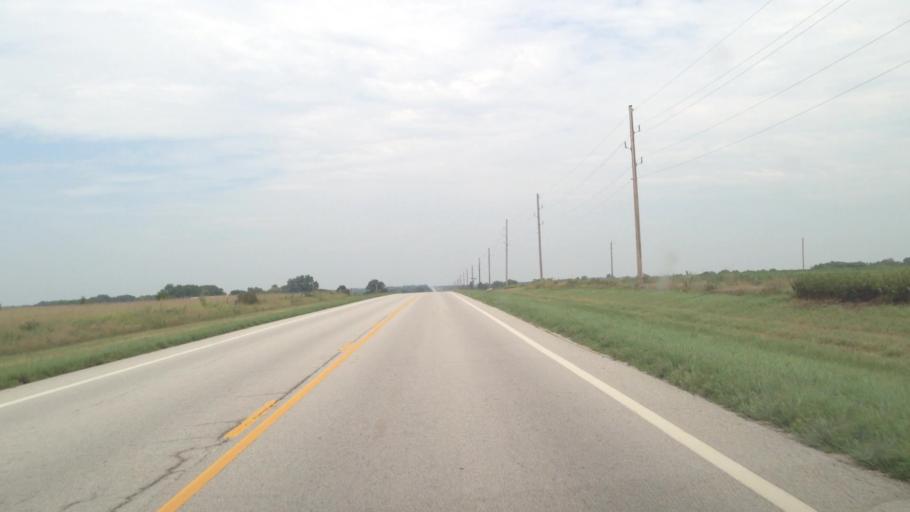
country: US
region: Kansas
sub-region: Allen County
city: Iola
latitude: 37.9342
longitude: -95.1700
